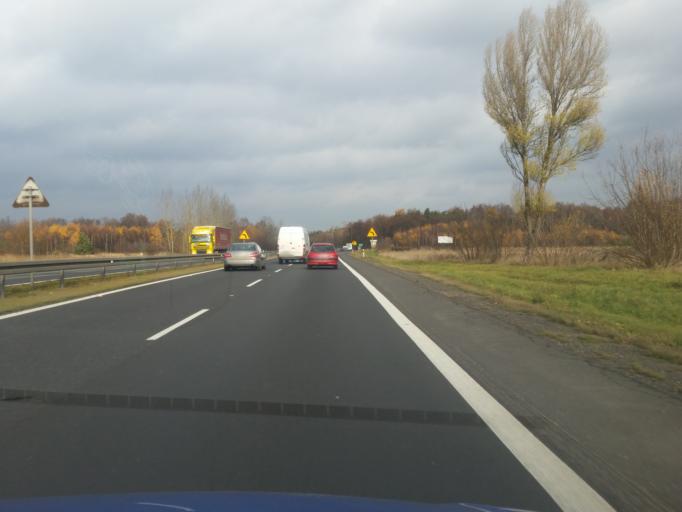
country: PL
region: Silesian Voivodeship
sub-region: Powiat czestochowski
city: Kamienica Polska
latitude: 50.6375
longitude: 19.1359
